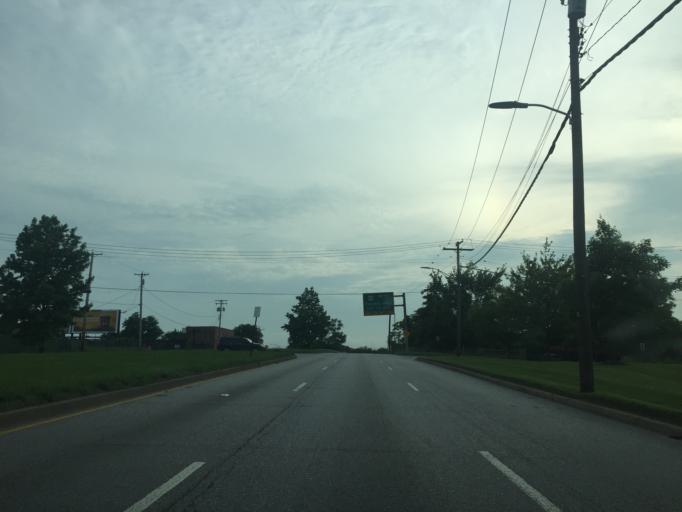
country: US
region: Maryland
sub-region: Baltimore County
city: Rosedale
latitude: 39.3007
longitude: -76.5457
